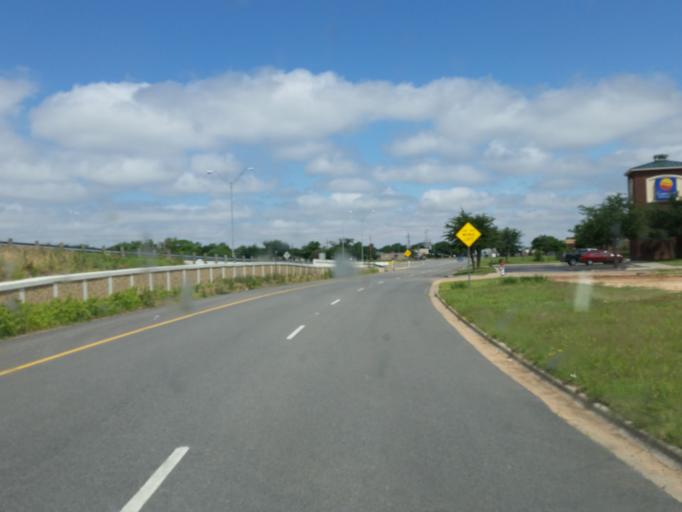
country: US
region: Texas
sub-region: Lubbock County
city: Lubbock
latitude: 33.5393
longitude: -101.8461
